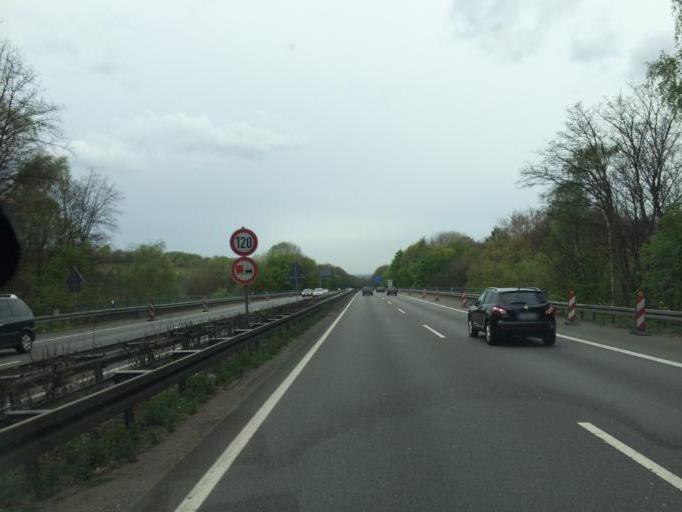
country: DE
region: North Rhine-Westphalia
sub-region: Regierungsbezirk Arnsberg
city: Herne
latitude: 51.5092
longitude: 7.2355
